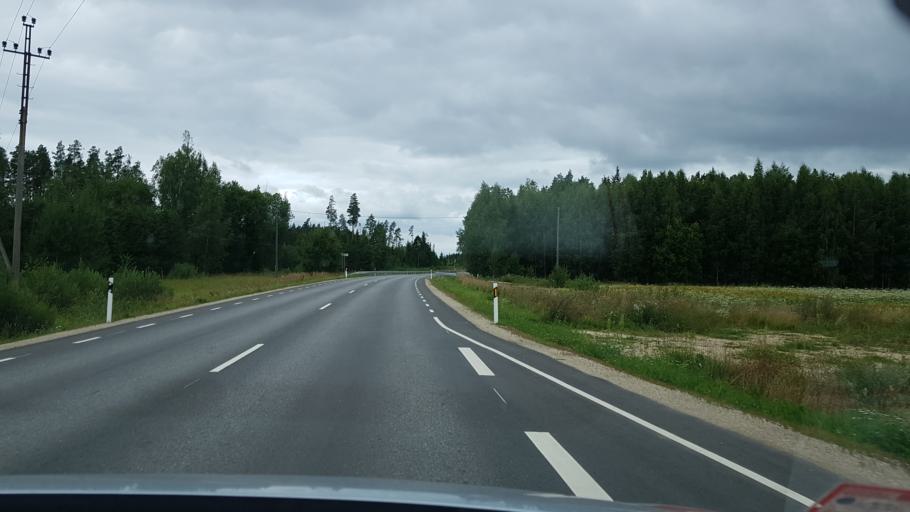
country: EE
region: Polvamaa
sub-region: Polva linn
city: Polva
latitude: 58.0818
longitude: 27.2386
